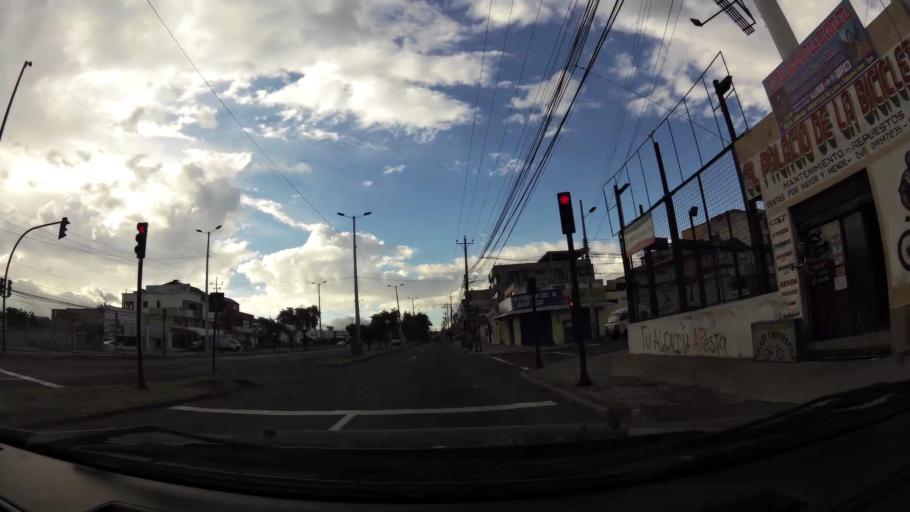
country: EC
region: Pichincha
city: Quito
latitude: -0.1387
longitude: -78.4824
